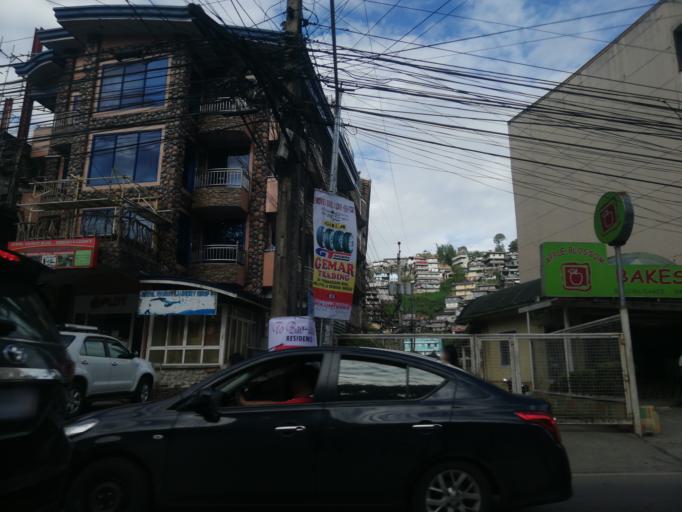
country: PH
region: Cordillera
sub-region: Province of Benguet
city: La Trinidad
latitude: 16.4413
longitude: 120.5937
